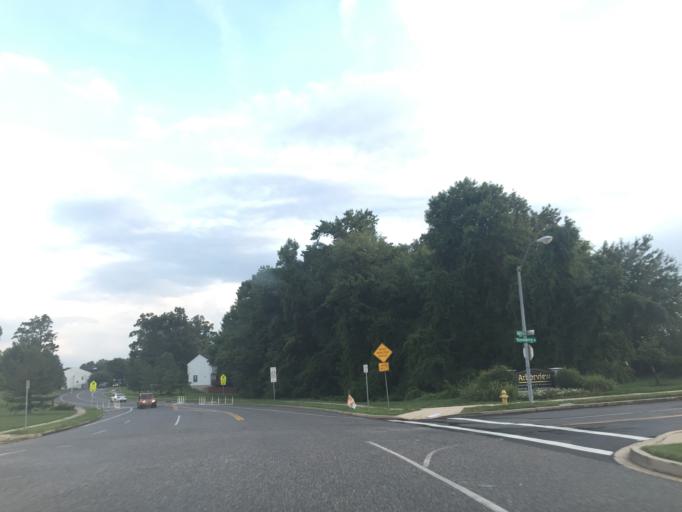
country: US
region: Maryland
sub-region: Harford County
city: Riverside
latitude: 39.4769
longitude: -76.2488
